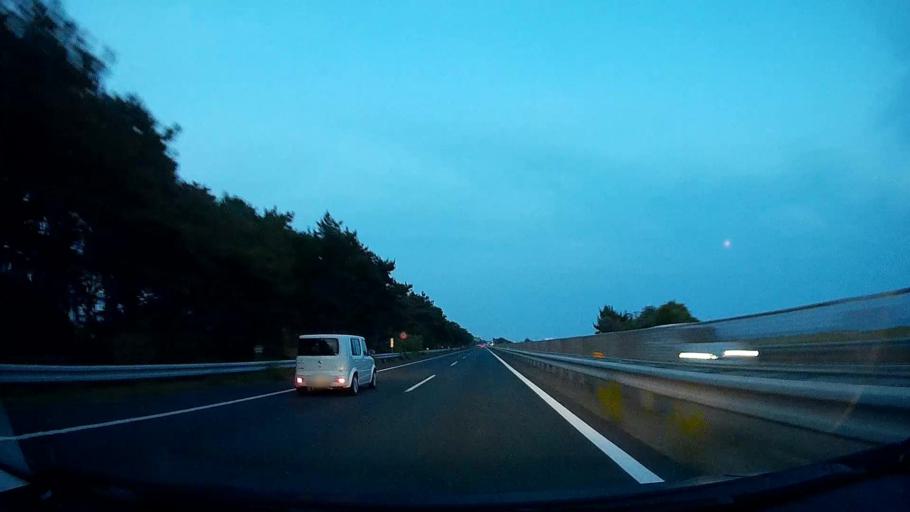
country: JP
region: Shizuoka
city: Kosai-shi
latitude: 34.6778
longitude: 137.6199
